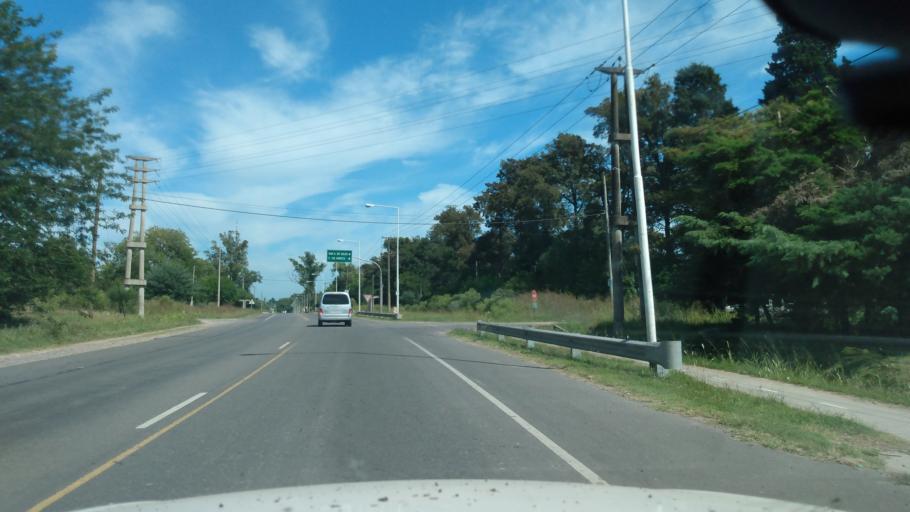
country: AR
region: Buenos Aires
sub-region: Partido de Lujan
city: Lujan
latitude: -34.5492
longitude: -59.1383
